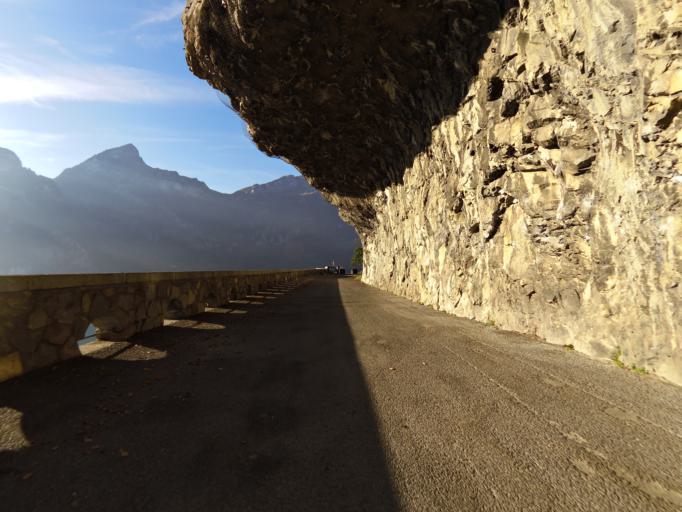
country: CH
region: Uri
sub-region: Uri
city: Flueelen
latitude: 46.9259
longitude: 8.6132
